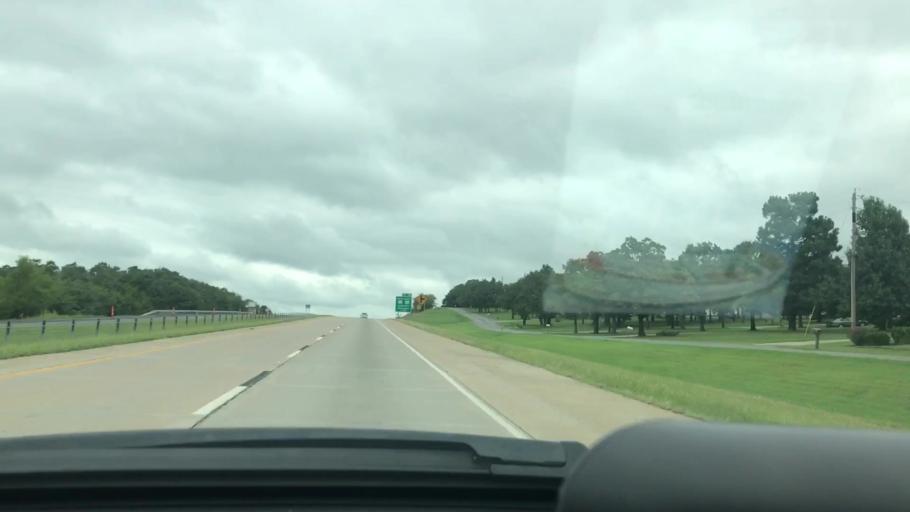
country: US
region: Oklahoma
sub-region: Pittsburg County
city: Krebs
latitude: 34.9860
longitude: -95.7221
